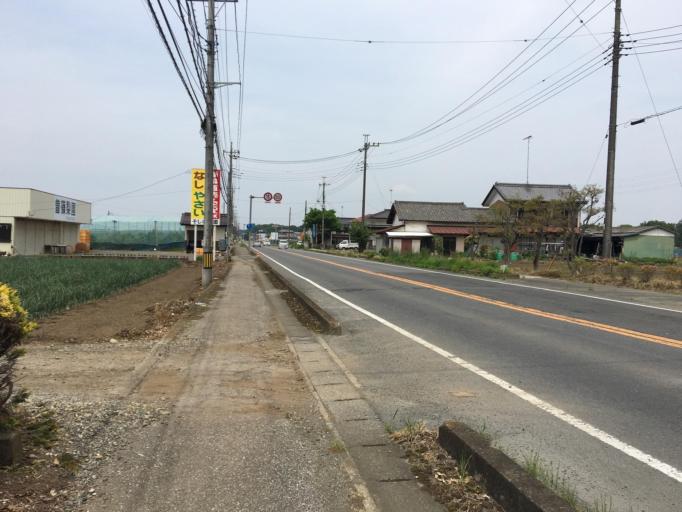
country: JP
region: Tochigi
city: Oyama
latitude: 36.3483
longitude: 139.8132
